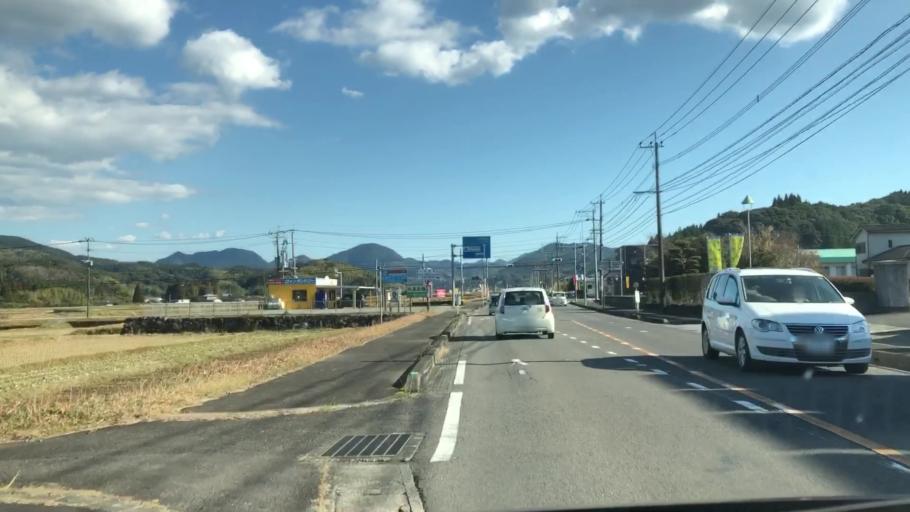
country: JP
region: Kagoshima
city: Satsumasendai
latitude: 31.7988
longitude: 130.4312
